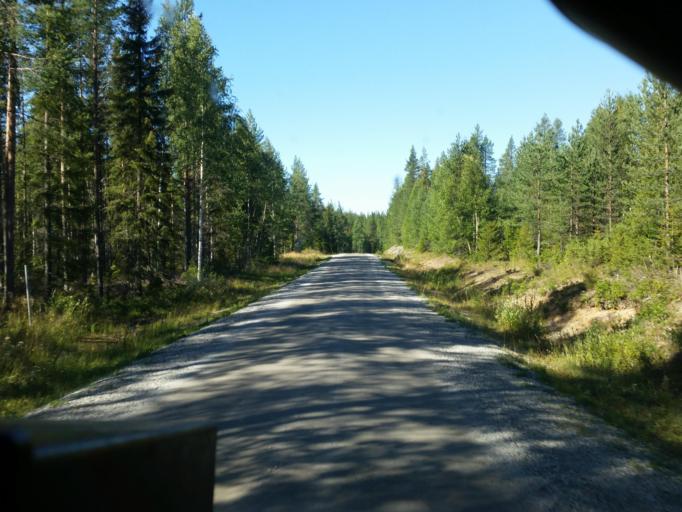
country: SE
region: Vaesterbotten
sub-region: Skelleftea Kommun
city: Storvik
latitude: 65.2145
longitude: 20.8307
